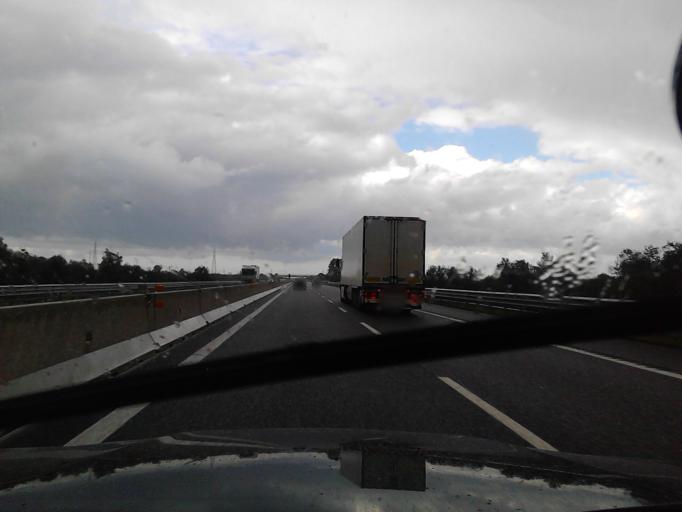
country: IT
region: Apulia
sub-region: Provincia di Bari
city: Molfetta
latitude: 41.1622
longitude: 16.6275
